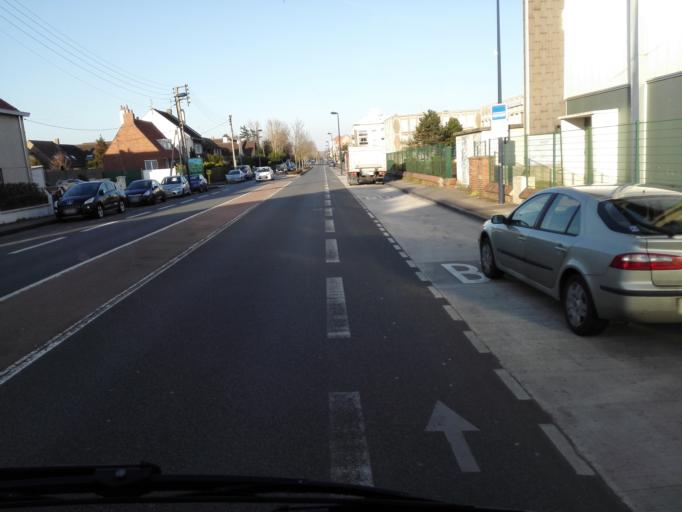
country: FR
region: Nord-Pas-de-Calais
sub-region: Departement du Nord
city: Coudekerque-Branche
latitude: 51.0483
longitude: 2.4177
